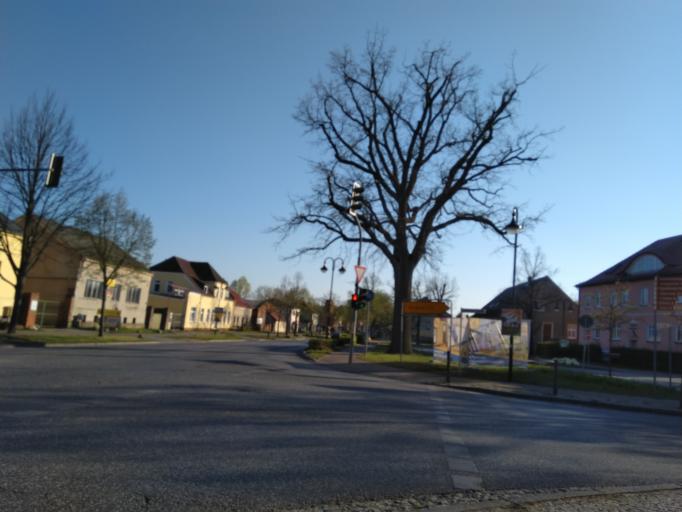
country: DE
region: Berlin
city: Buch
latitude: 52.6547
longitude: 13.5431
